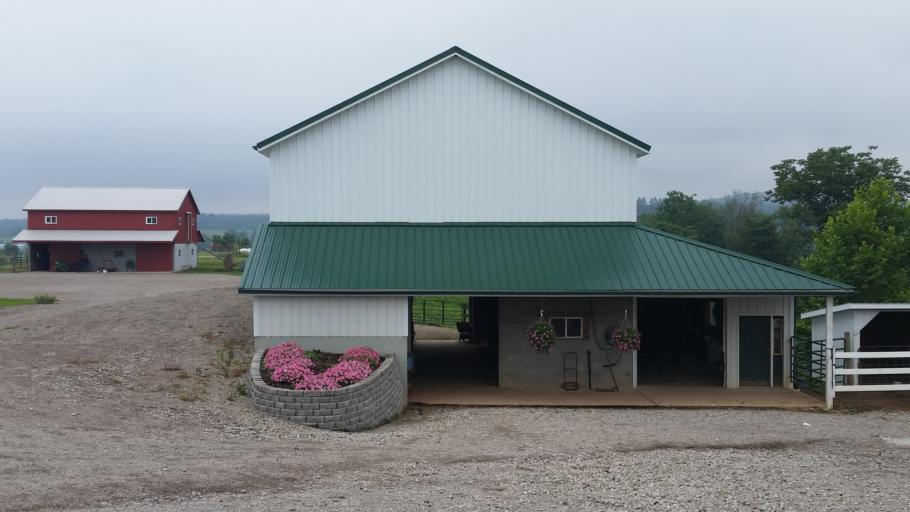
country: US
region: Ohio
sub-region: Gallia County
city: Gallipolis
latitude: 38.7675
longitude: -82.3793
